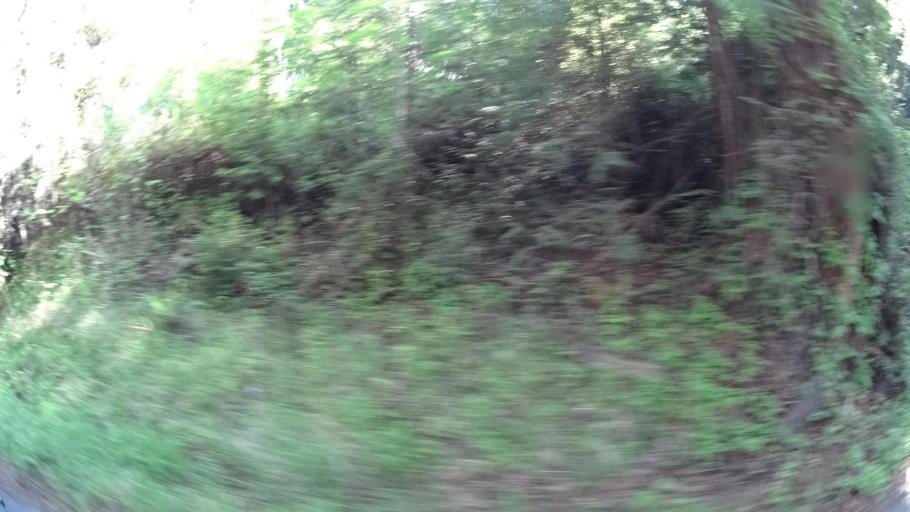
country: US
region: California
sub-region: Humboldt County
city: Rio Dell
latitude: 40.4589
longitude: -124.0395
